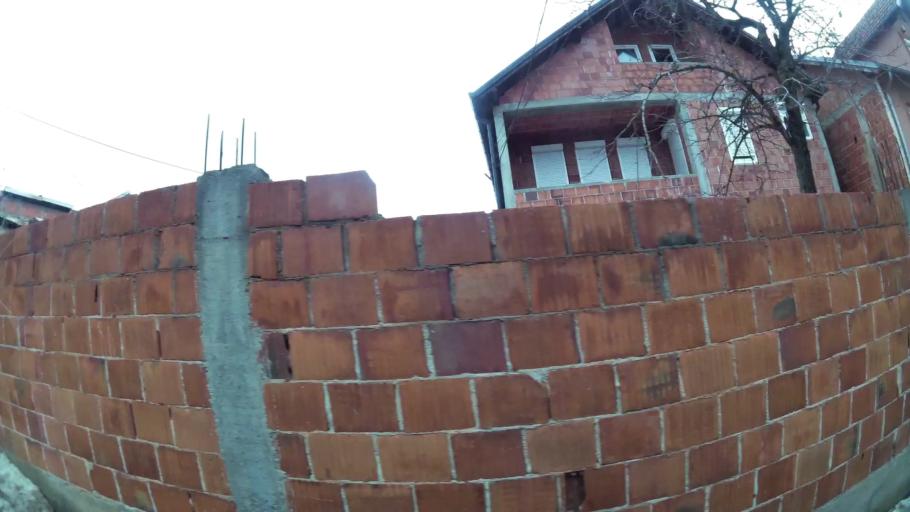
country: XK
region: Pristina
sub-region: Komuna e Prishtines
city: Pristina
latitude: 42.6814
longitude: 21.1665
